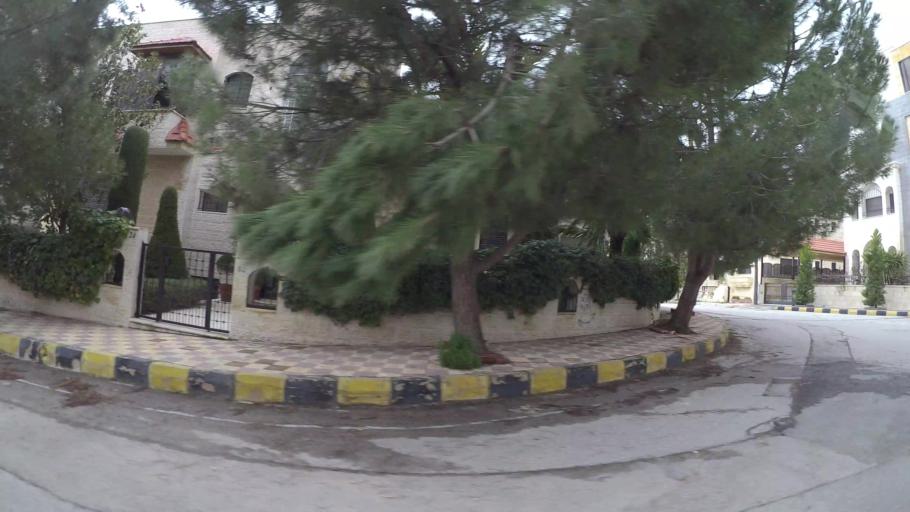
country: JO
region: Amman
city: Wadi as Sir
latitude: 31.9663
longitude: 35.8299
